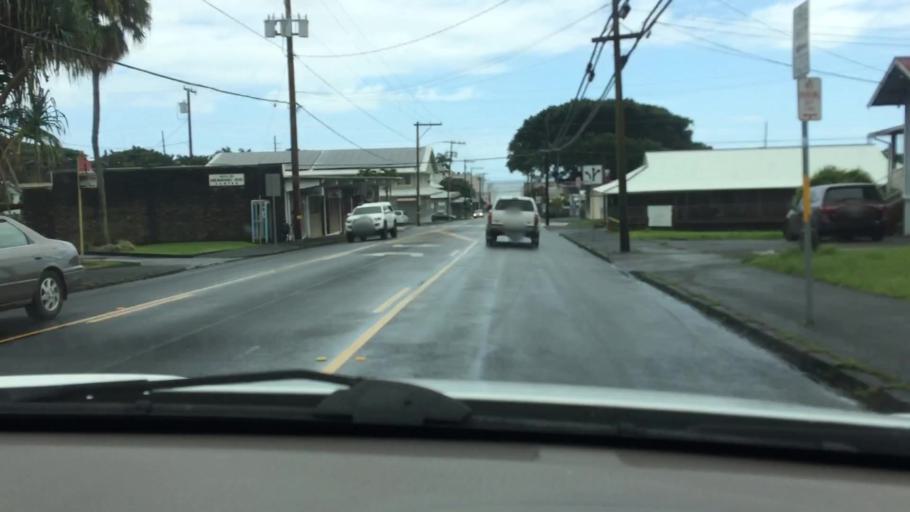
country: US
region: Hawaii
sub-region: Hawaii County
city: Hilo
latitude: 19.7242
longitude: -155.0906
